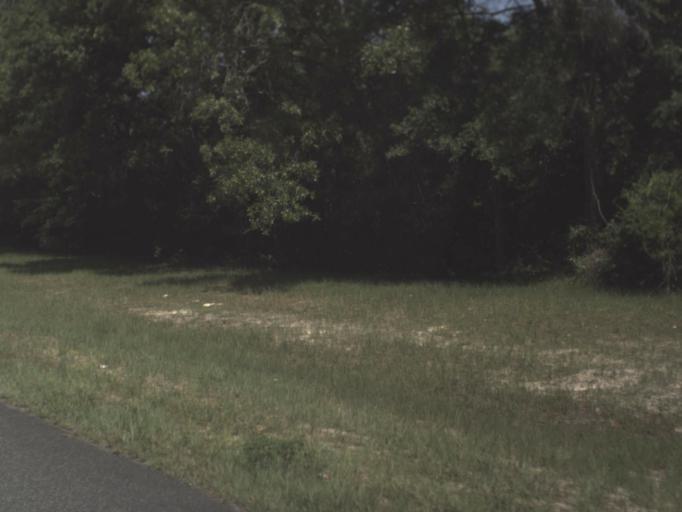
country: US
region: Florida
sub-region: Clay County
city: Asbury Lake
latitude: 29.9780
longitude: -81.8591
